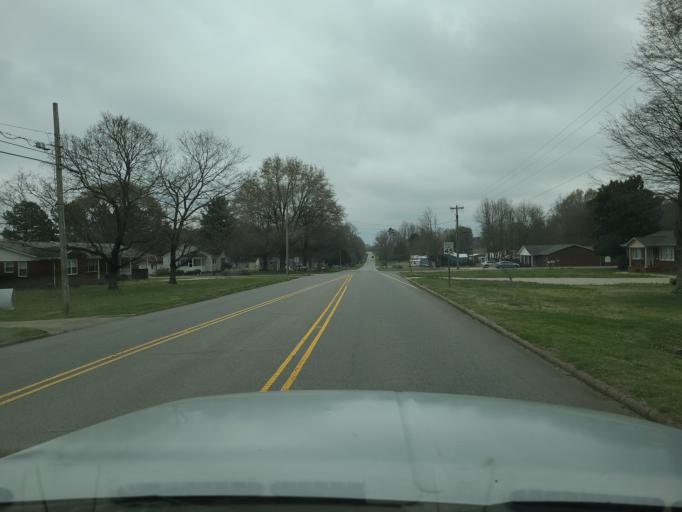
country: US
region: North Carolina
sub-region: Cleveland County
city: Shelby
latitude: 35.4113
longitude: -81.6412
